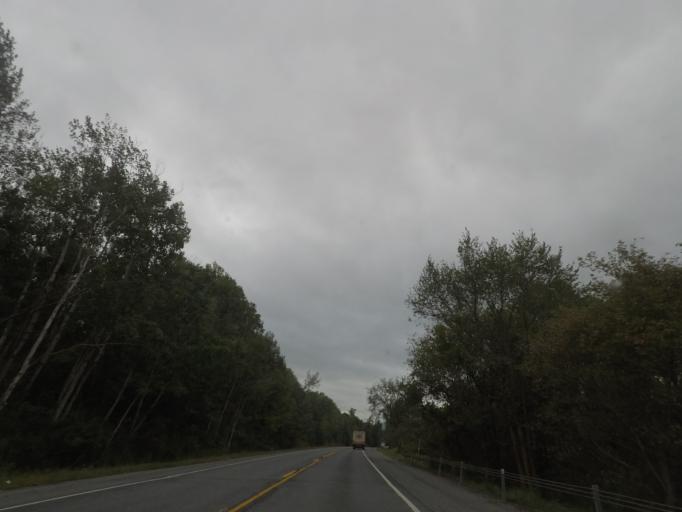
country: US
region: New York
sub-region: Rensselaer County
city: Hoosick Falls
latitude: 42.9423
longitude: -73.3670
